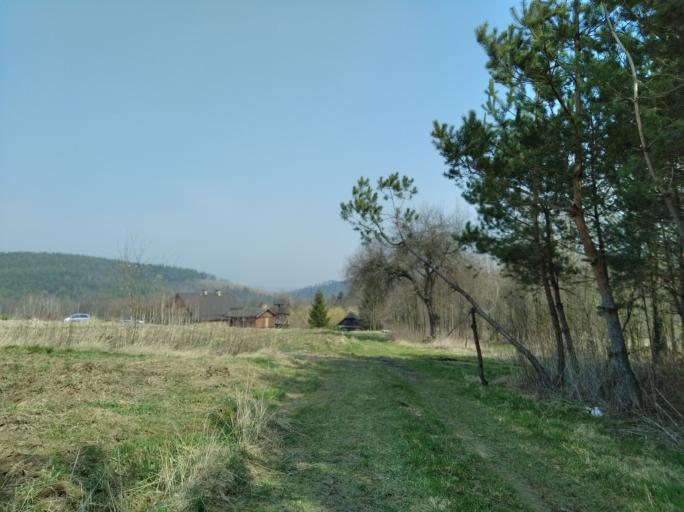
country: PL
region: Subcarpathian Voivodeship
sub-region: Powiat krosnienski
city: Korczyna
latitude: 49.7935
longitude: 21.8187
